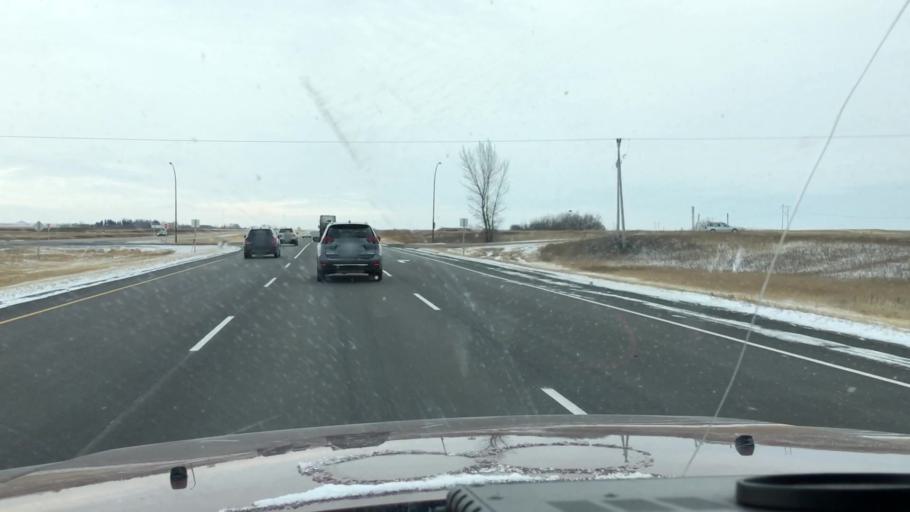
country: CA
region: Saskatchewan
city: Saskatoon
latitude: 51.8539
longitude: -106.5107
